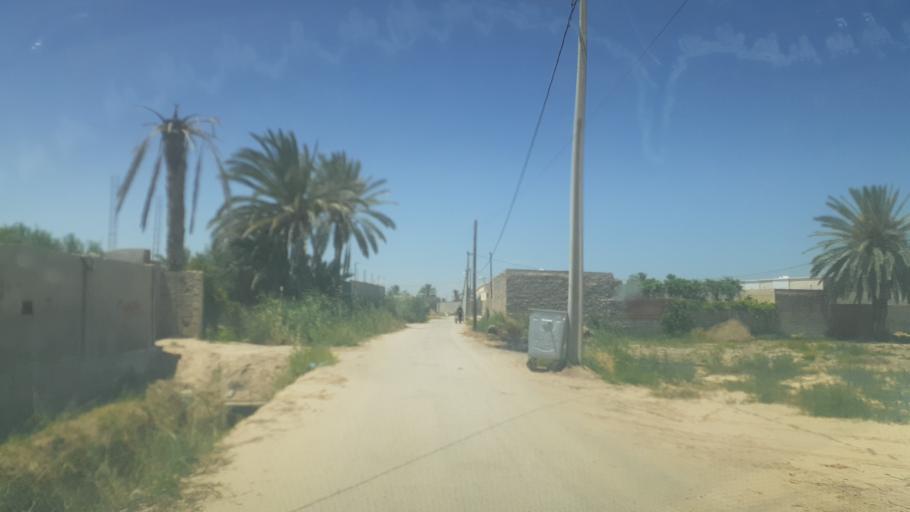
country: TN
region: Qabis
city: Gabes
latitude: 33.9303
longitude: 10.0594
